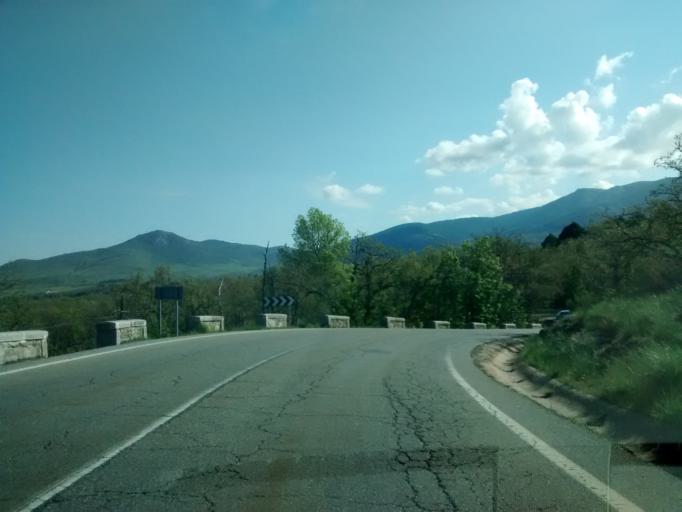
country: ES
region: Castille and Leon
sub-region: Provincia de Segovia
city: San Ildefonso
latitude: 40.8836
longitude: -4.0189
